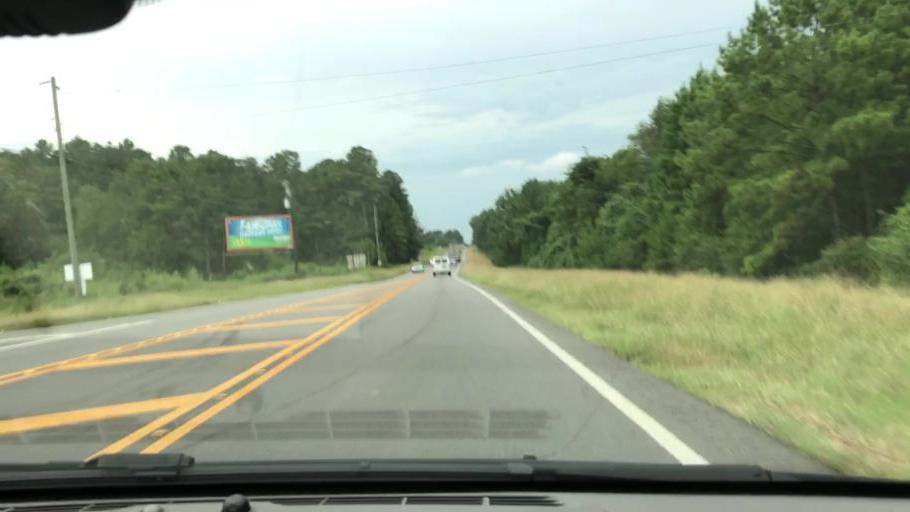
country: US
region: Alabama
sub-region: Houston County
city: Webb
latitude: 31.2894
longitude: -85.1327
